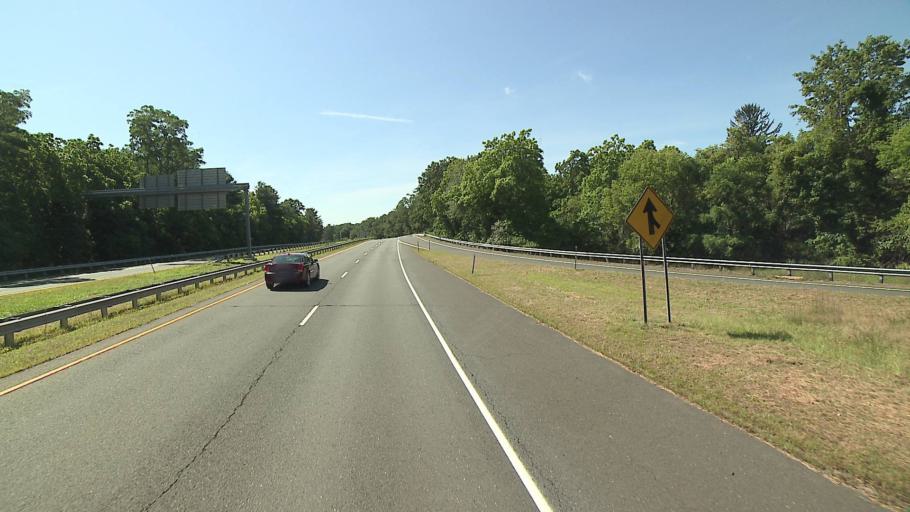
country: US
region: Connecticut
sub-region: Hartford County
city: Tariffville
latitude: 41.8895
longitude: -72.7489
